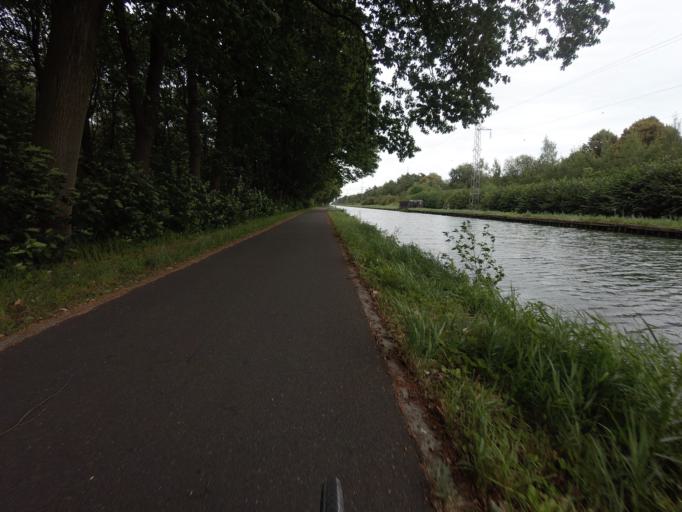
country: BE
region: Flanders
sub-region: Provincie Antwerpen
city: Brecht
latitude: 51.3107
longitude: 4.5902
